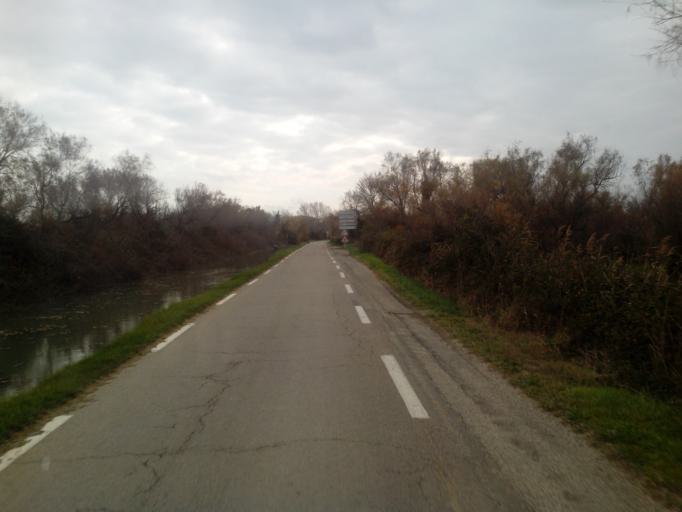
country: FR
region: Languedoc-Roussillon
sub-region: Departement du Gard
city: Vauvert
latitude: 43.6073
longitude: 4.3346
